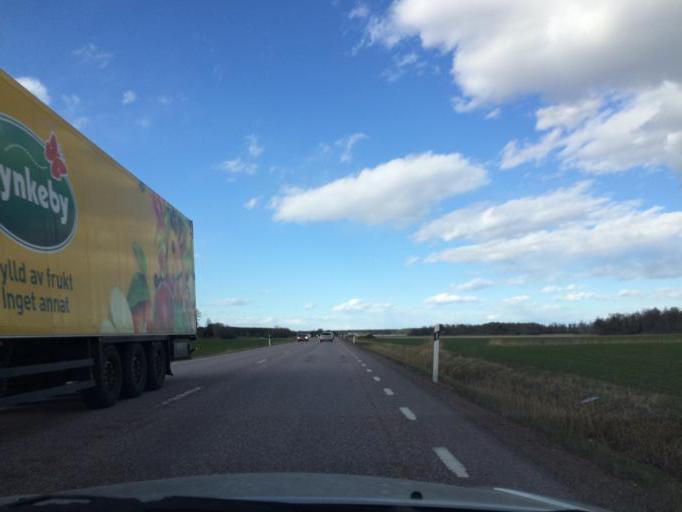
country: SE
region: Vaestmanland
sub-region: Hallstahammars Kommun
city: Kolback
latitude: 59.5374
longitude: 16.3230
